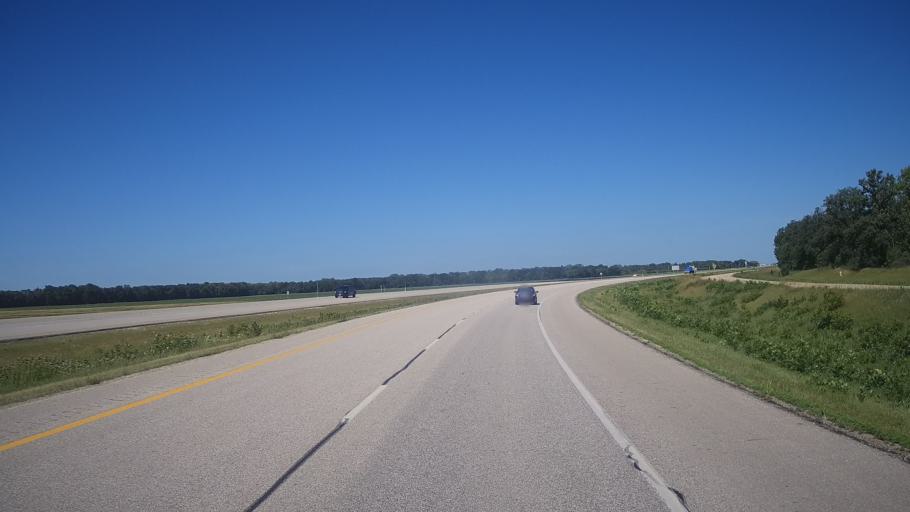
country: CA
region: Manitoba
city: Portage la Prairie
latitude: 49.9464
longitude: -98.2993
